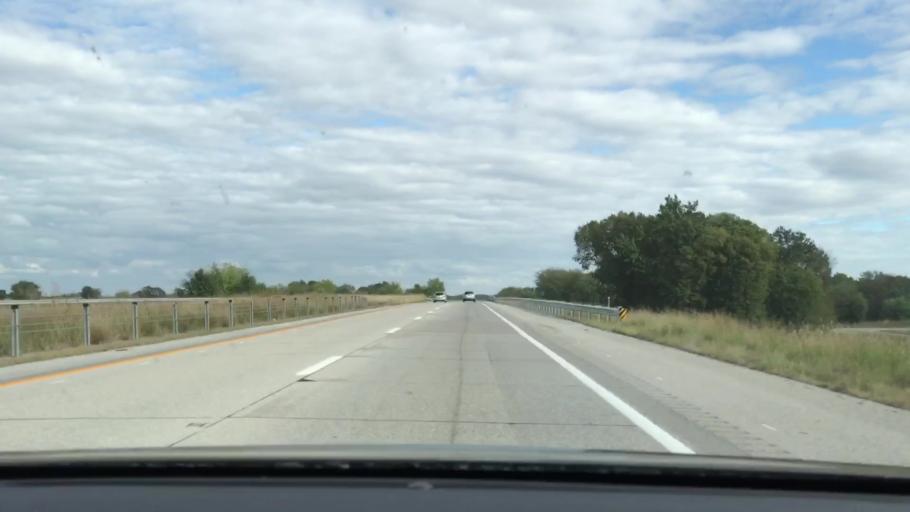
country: US
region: Kentucky
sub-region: Christian County
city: Hopkinsville
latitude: 36.8163
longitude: -87.6360
